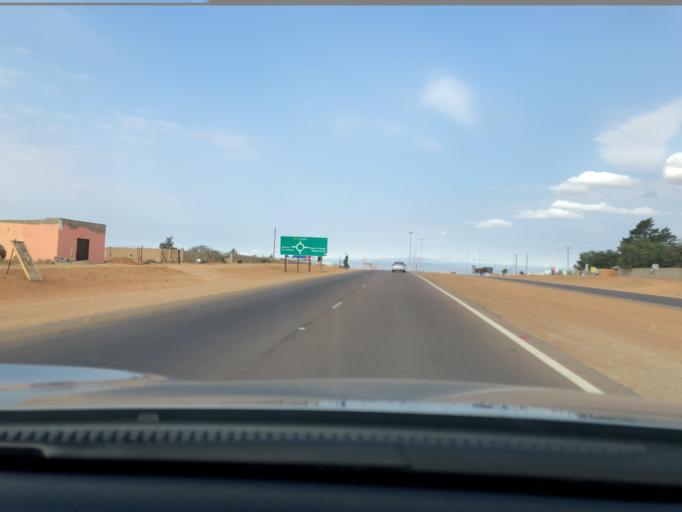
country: ZA
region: Limpopo
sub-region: Capricorn District Municipality
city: Mankoeng
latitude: -23.8899
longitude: 29.6656
